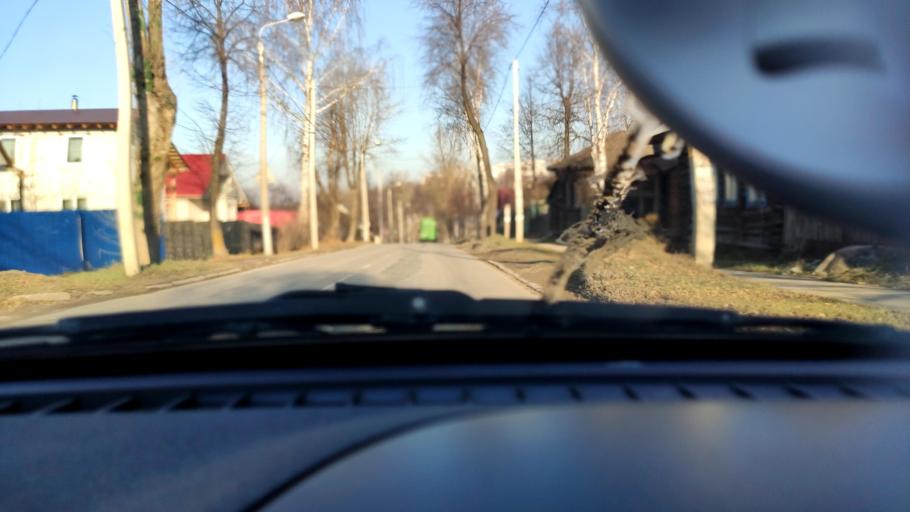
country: RU
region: Perm
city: Perm
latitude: 58.0246
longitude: 56.3131
